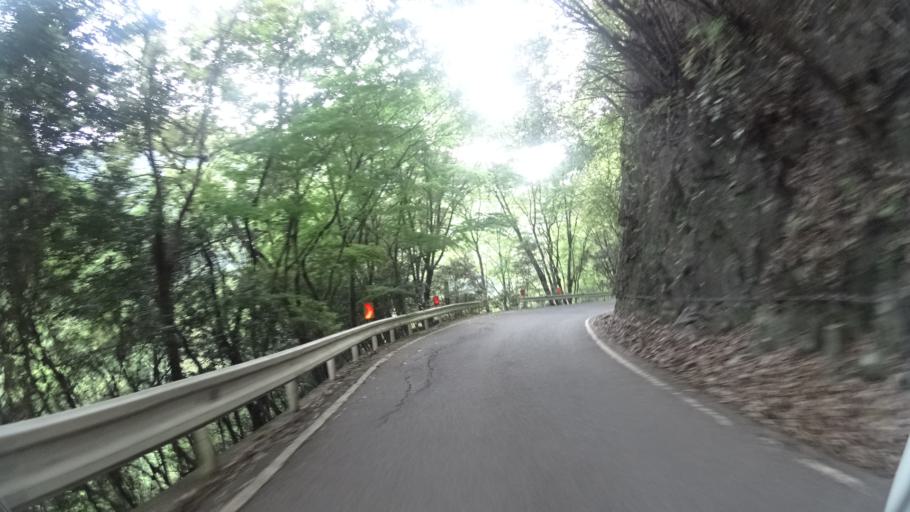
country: JP
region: Tokushima
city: Ikedacho
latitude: 33.9362
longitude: 133.8185
